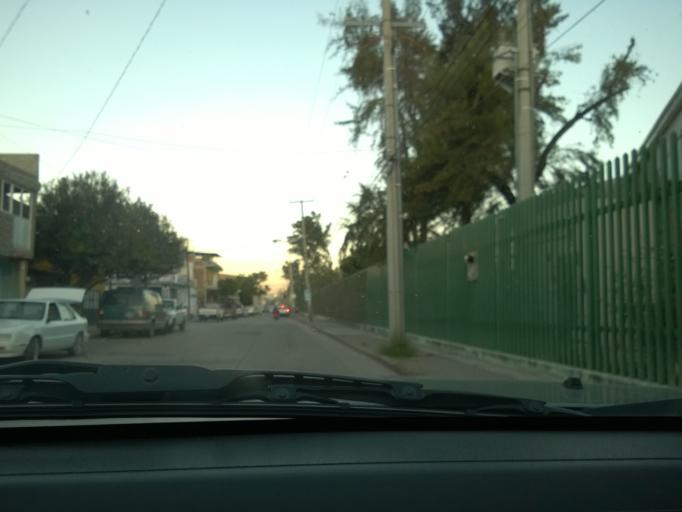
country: MX
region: Guanajuato
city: Leon
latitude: 21.1253
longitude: -101.6582
